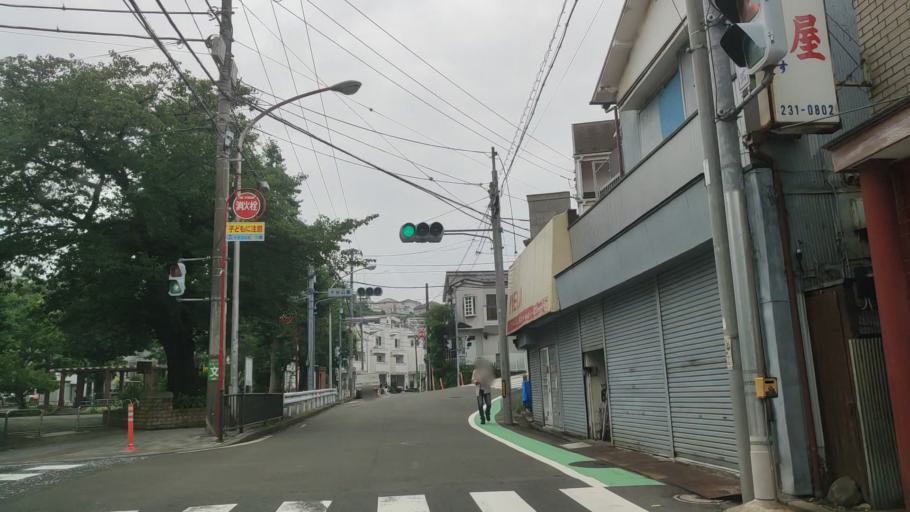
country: JP
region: Kanagawa
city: Yokohama
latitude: 35.4495
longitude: 139.6106
